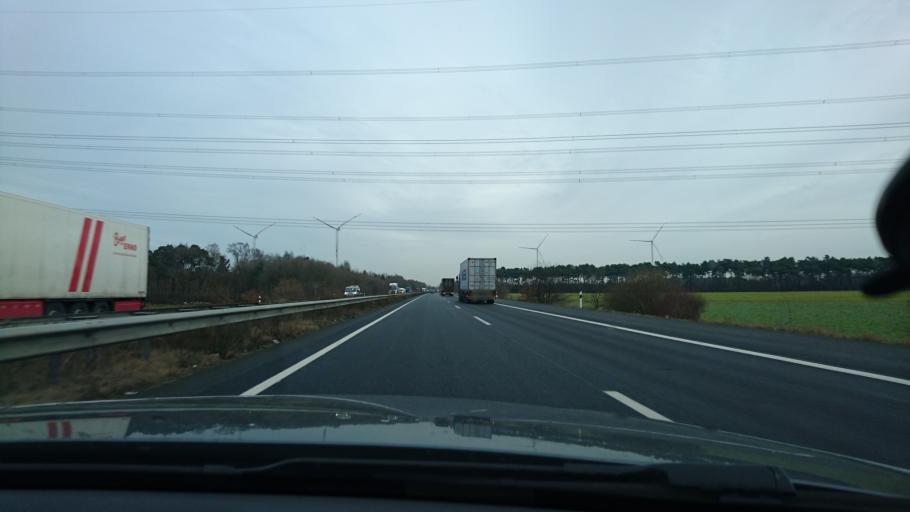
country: DE
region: Lower Saxony
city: Rieste
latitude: 52.4476
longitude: 8.0389
